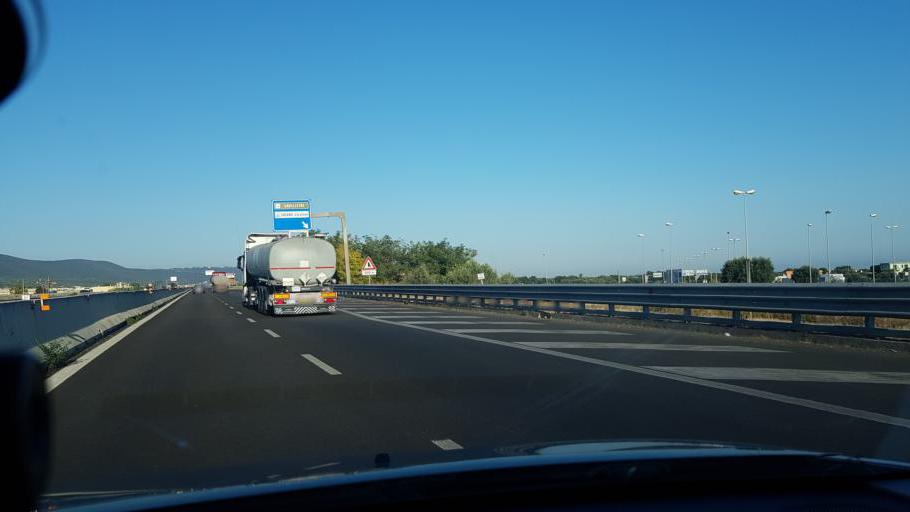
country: IT
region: Apulia
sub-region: Provincia di Brindisi
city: Fasano
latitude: 40.8388
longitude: 17.3776
